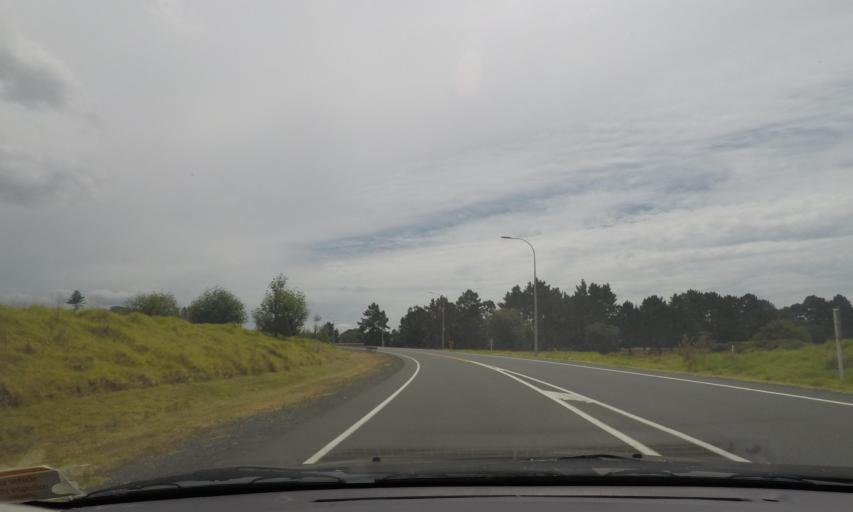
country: NZ
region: Auckland
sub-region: Auckland
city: Mangere
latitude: -36.9957
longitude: 174.7994
